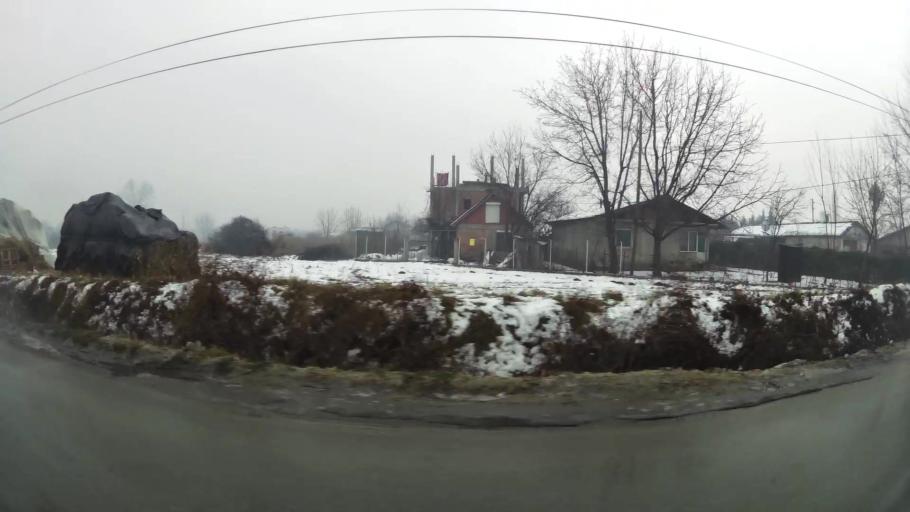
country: MK
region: Ilinden
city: Idrizovo
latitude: 41.9544
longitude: 21.5801
